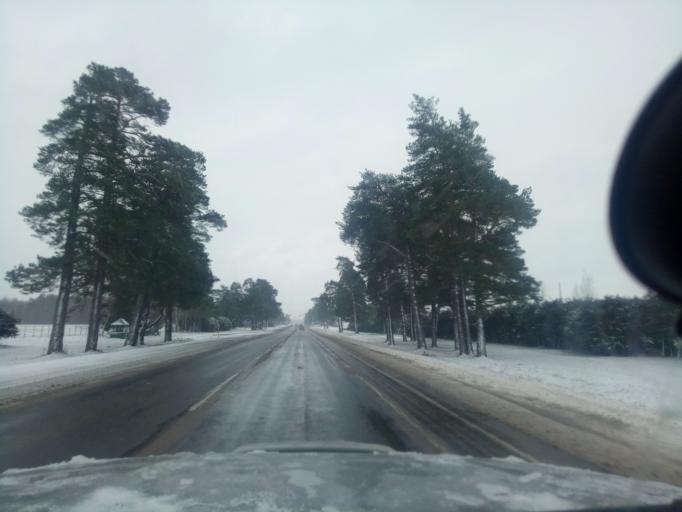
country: BY
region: Minsk
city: Nyasvizh
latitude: 53.2493
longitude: 26.6224
